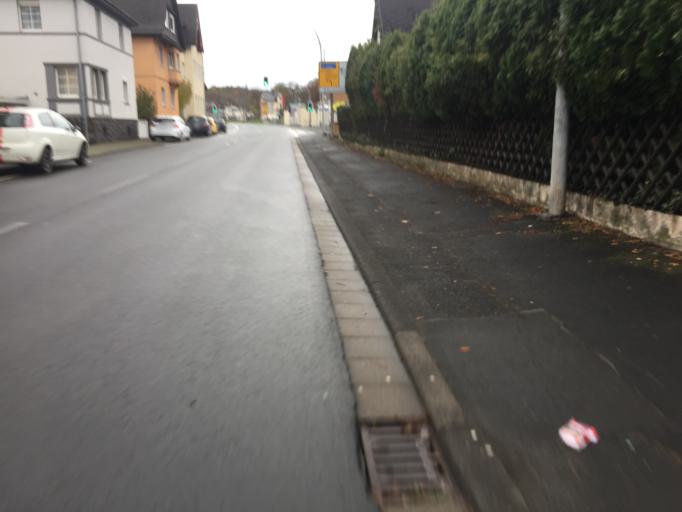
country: DE
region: Hesse
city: Dillenburg
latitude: 50.7419
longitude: 8.2864
